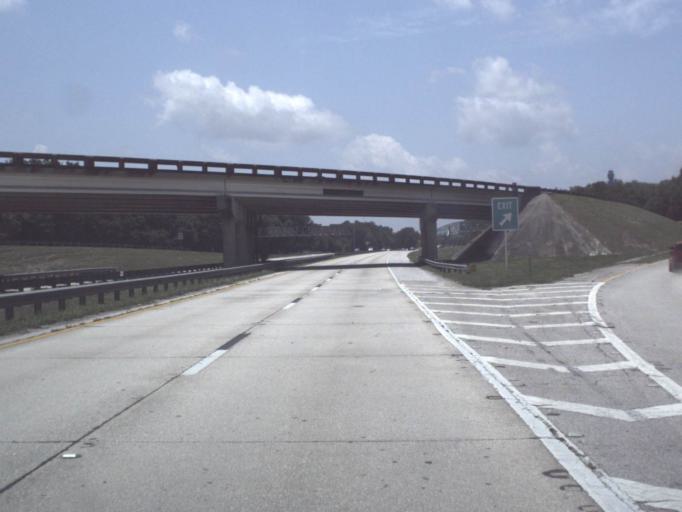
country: US
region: Florida
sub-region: Duval County
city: Jacksonville
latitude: 30.3021
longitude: -81.6113
